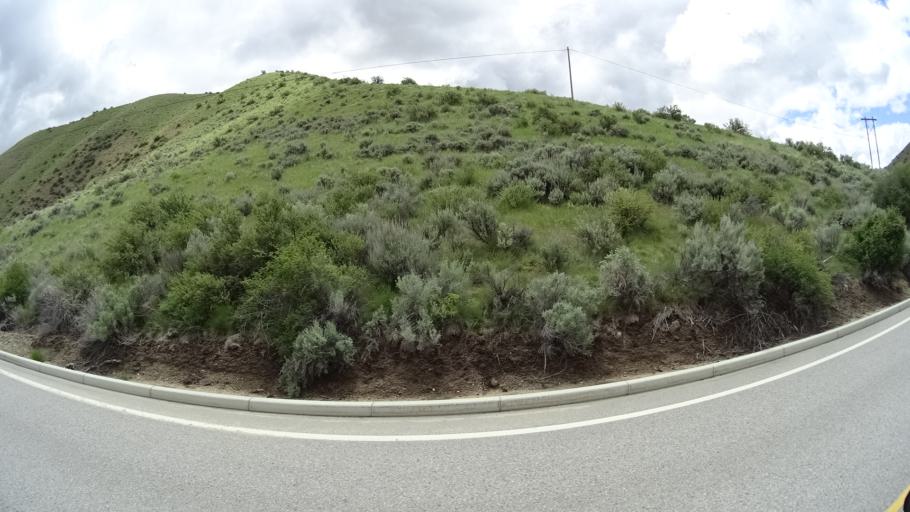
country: US
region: Idaho
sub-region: Ada County
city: Boise
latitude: 43.6868
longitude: -116.1834
